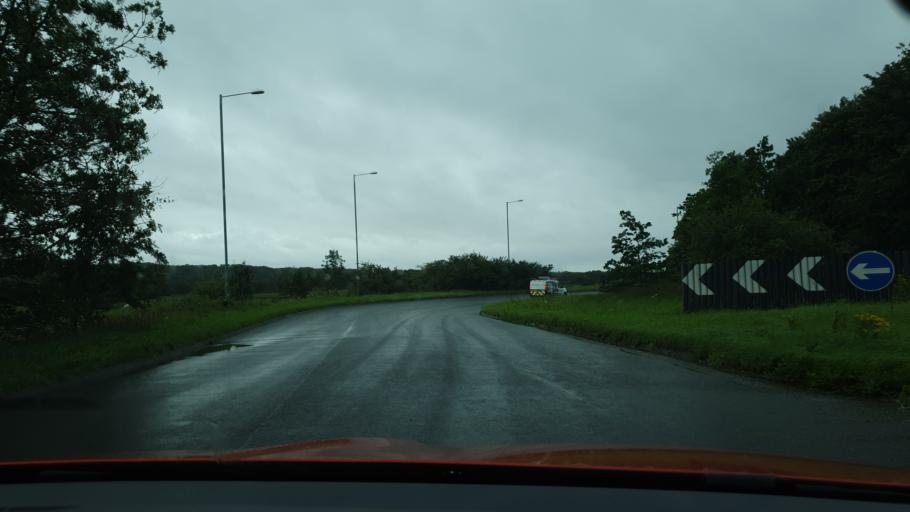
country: GB
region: England
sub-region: Cumbria
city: Arnside
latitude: 54.2261
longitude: -2.8697
